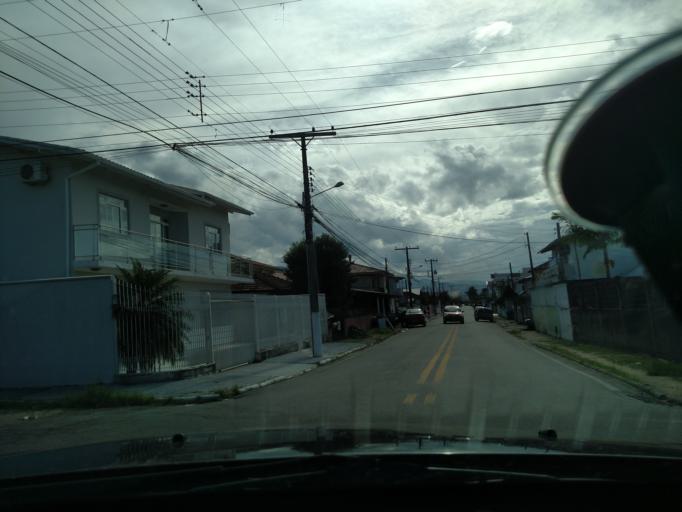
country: BR
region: Santa Catarina
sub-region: Sao Jose
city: Campinas
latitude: -27.6042
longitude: -48.6450
